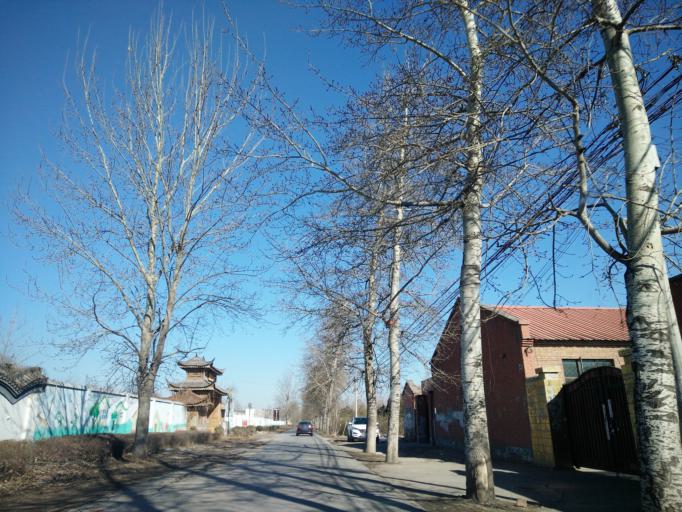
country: CN
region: Beijing
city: Yinghai
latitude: 39.7455
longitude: 116.4559
